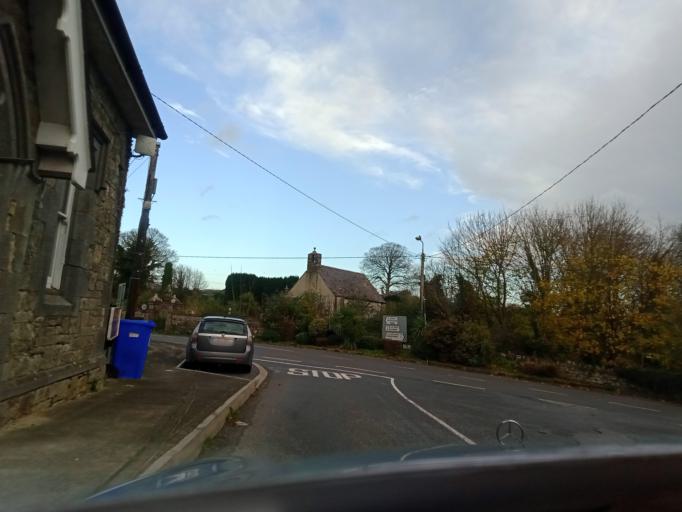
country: IE
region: Leinster
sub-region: Kilkenny
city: Piltown
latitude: 52.3282
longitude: -7.3155
